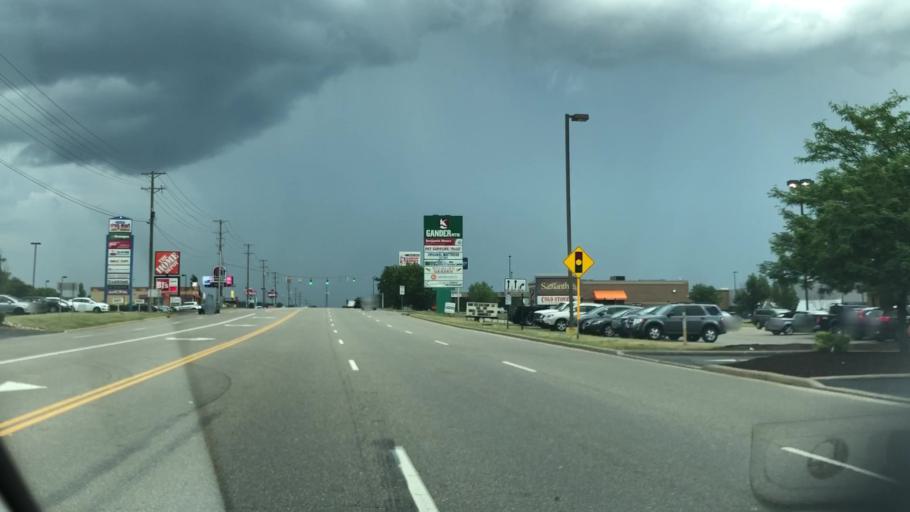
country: US
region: Ohio
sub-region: Stark County
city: North Canton
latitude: 40.8793
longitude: -81.4405
